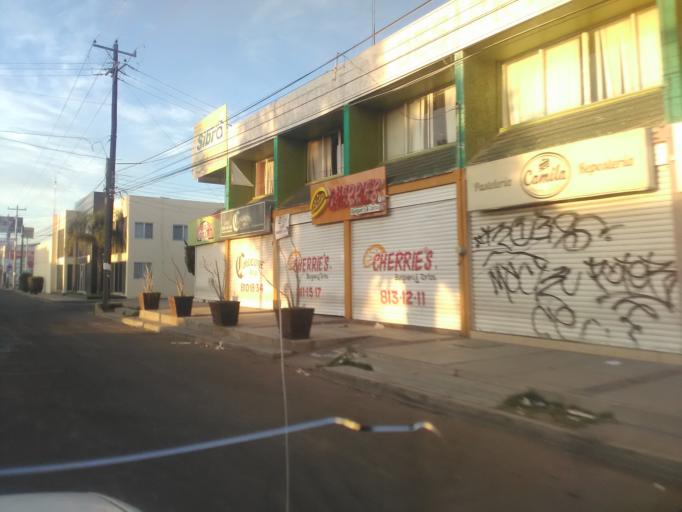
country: MX
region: Durango
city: Victoria de Durango
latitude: 24.0022
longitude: -104.6625
